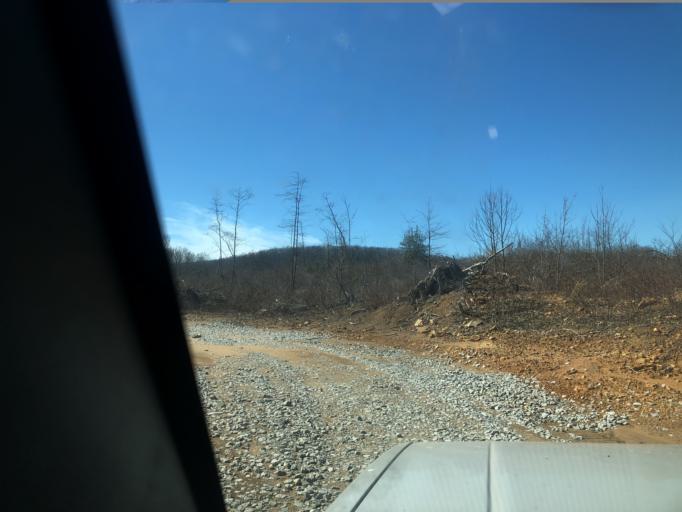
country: US
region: Tennessee
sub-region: Roane County
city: Rockwood
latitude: 35.9736
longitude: -84.7520
